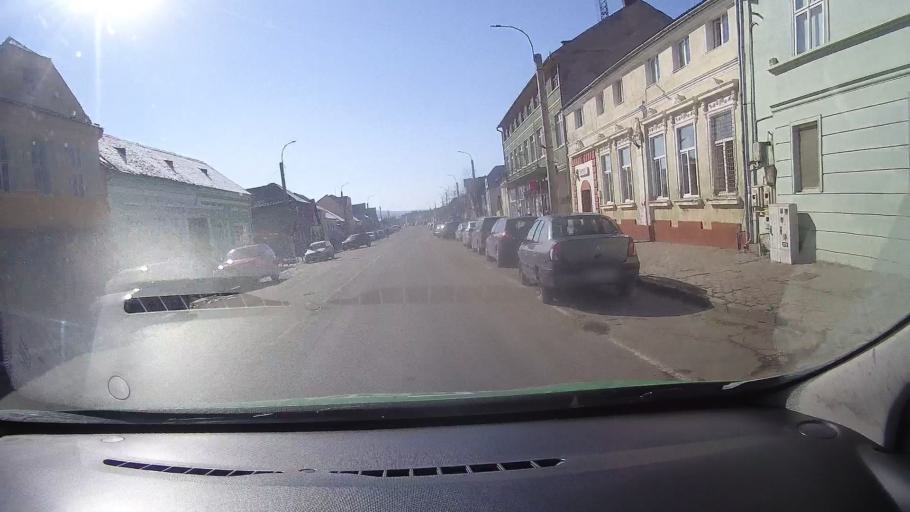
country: RO
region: Brasov
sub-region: Oras Rupea
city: Rupea
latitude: 46.0374
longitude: 25.2198
